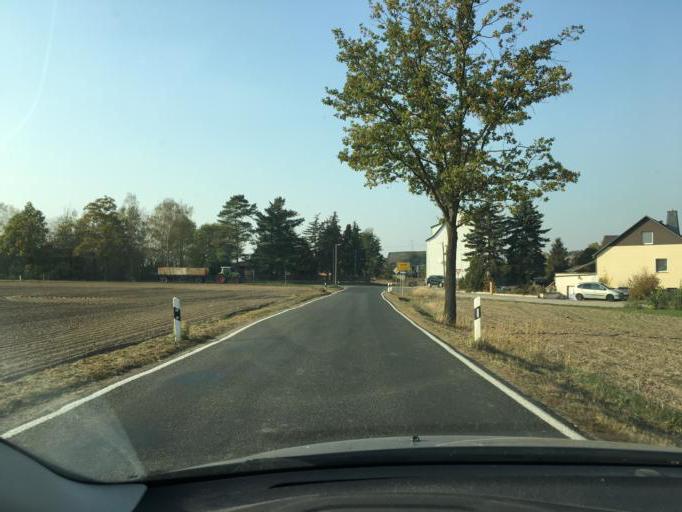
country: DE
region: Saxony
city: Wurzen
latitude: 51.3401
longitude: 12.7686
